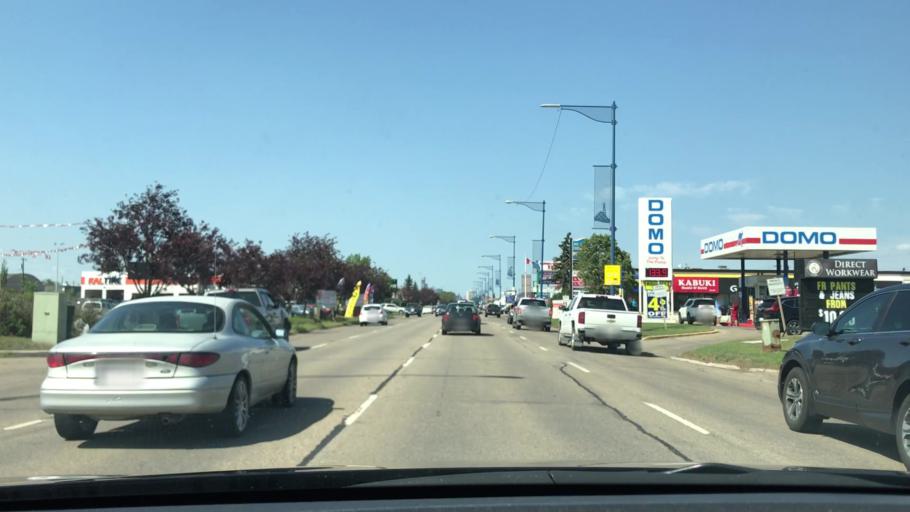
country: CA
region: Alberta
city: Edmonton
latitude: 53.4915
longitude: -113.4920
